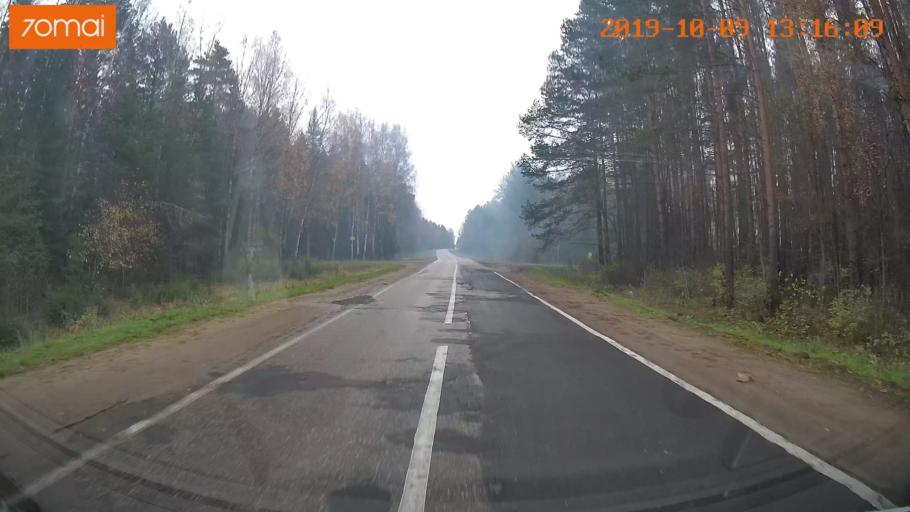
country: RU
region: Jaroslavl
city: Lyubim
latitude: 58.3631
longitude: 40.7621
